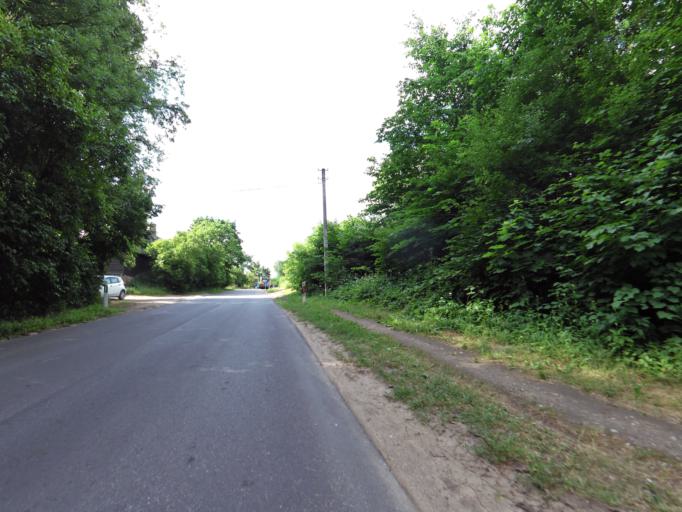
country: LT
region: Vilnius County
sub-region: Vilnius
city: Fabijoniskes
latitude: 54.7426
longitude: 25.2902
